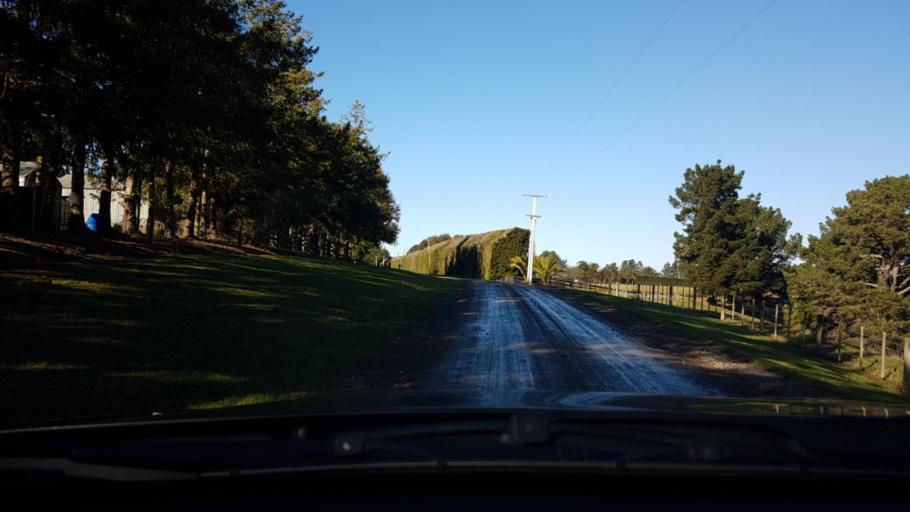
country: NZ
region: Canterbury
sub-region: Waimakariri District
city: Woodend
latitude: -43.2503
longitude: 172.5764
